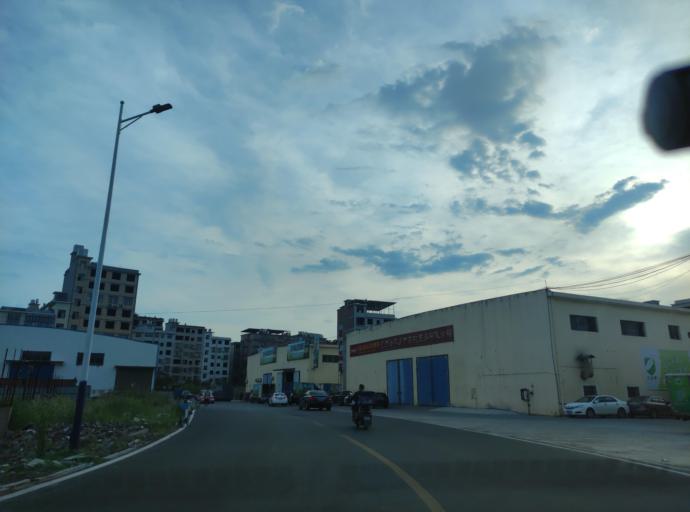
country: CN
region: Jiangxi Sheng
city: Pingxiang
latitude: 27.6419
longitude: 113.8799
